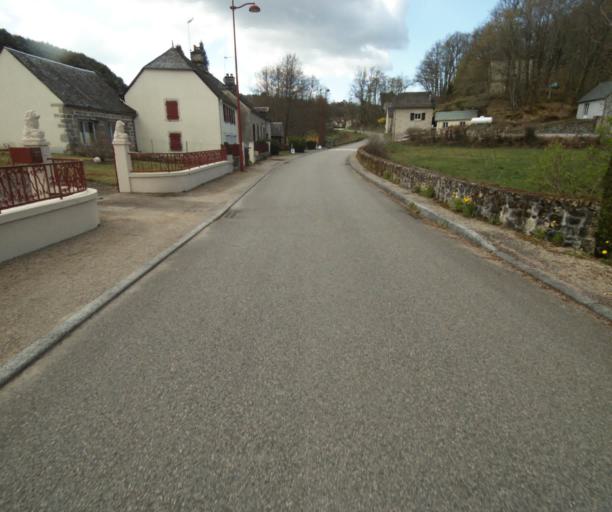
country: FR
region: Limousin
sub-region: Departement de la Correze
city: Laguenne
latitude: 45.2292
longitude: 1.8970
